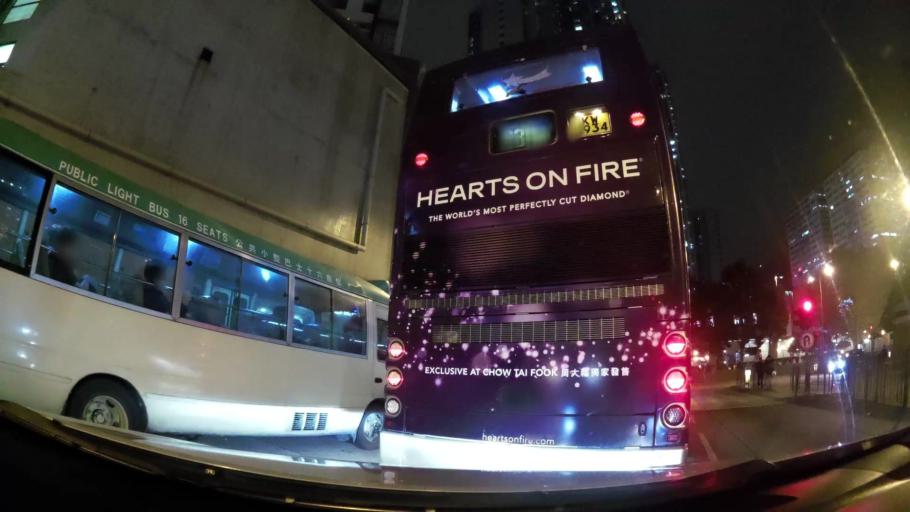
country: HK
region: Tsuen Wan
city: Tsuen Wan
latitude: 22.3572
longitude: 114.1289
